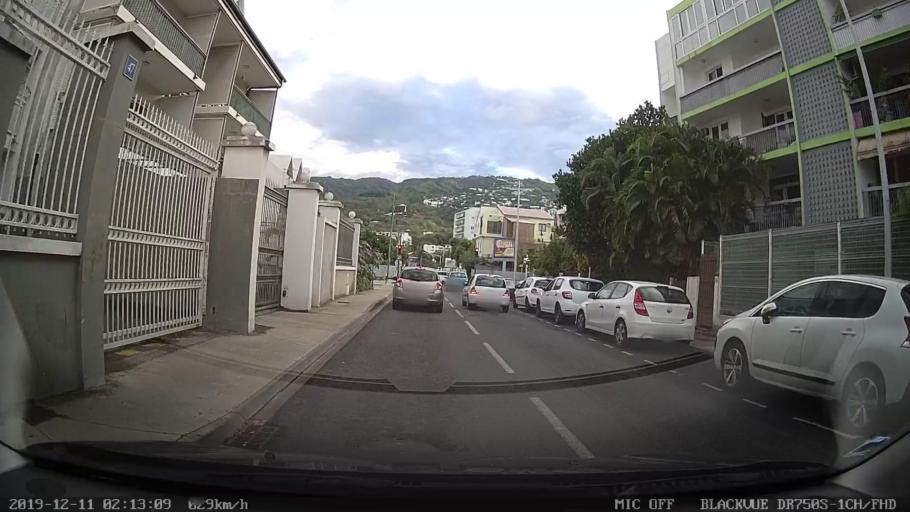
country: RE
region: Reunion
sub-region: Reunion
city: Saint-Denis
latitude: -20.8886
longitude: 55.4534
